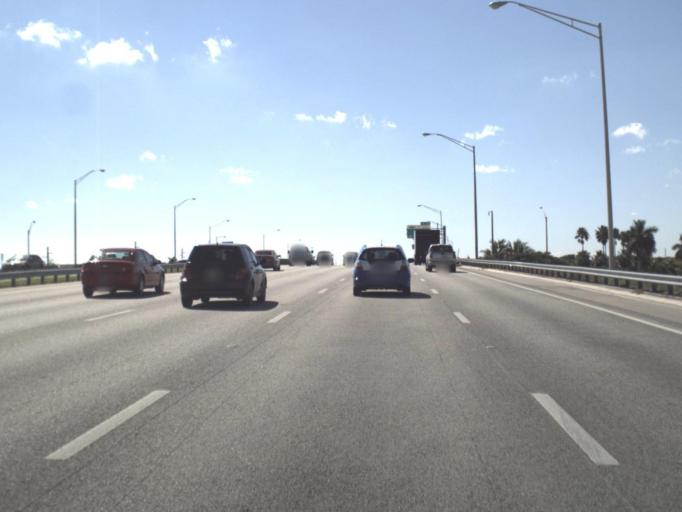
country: US
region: Florida
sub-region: Miami-Dade County
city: Sweetwater
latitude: 25.7626
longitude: -80.3856
